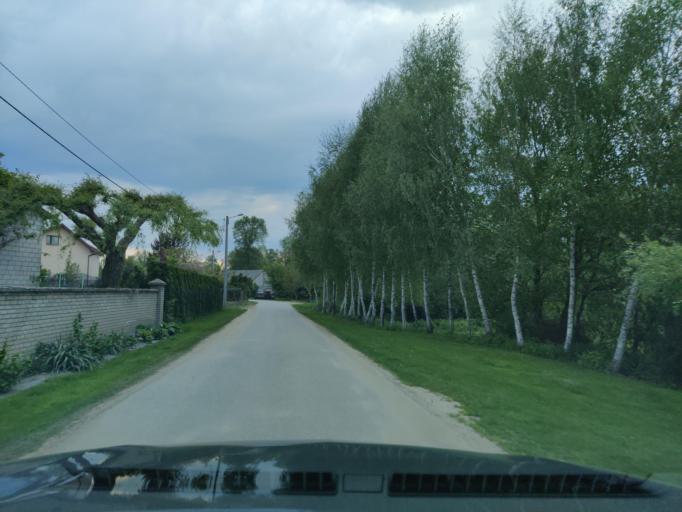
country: PL
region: Masovian Voivodeship
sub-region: Powiat piaseczynski
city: Konstancin-Jeziorna
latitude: 52.1193
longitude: 21.1668
